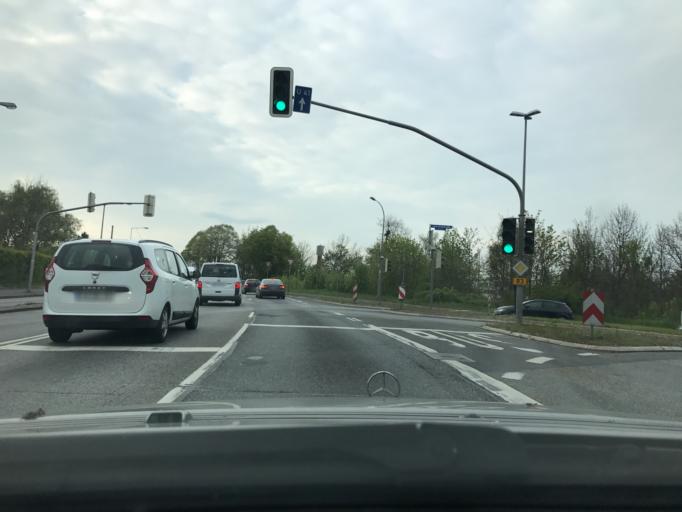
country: DE
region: Hesse
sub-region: Regierungsbezirk Kassel
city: Kassel
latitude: 51.3032
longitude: 9.5168
